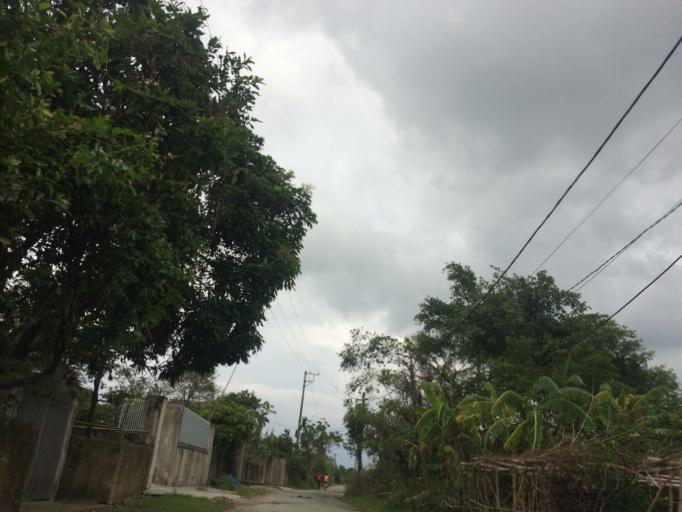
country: VN
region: Ha Tinh
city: Ha Tinh
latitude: 18.3252
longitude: 105.9194
